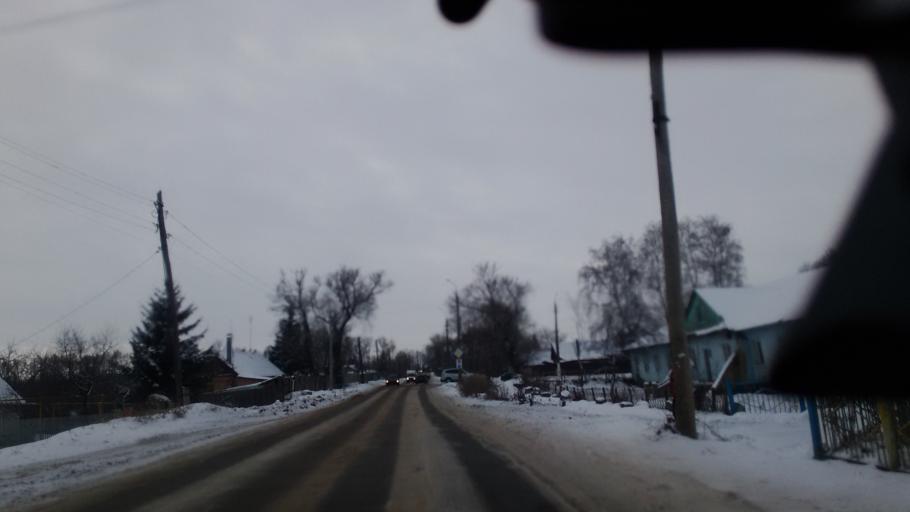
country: RU
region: Tula
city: Bogoroditsk
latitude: 53.7664
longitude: 38.1110
